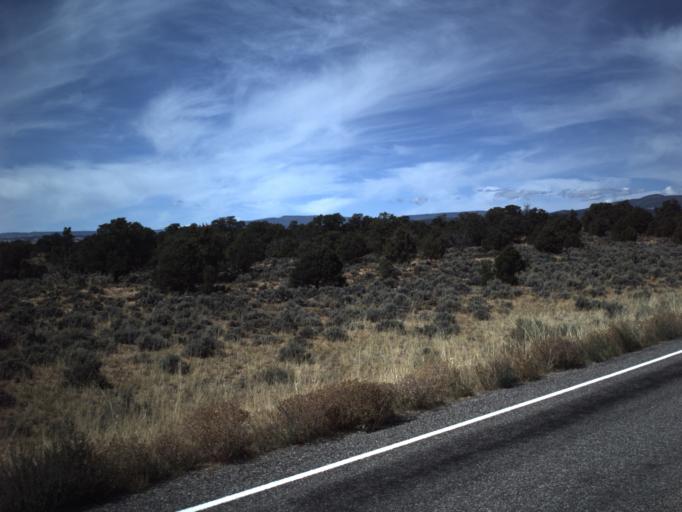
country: US
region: Utah
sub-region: Wayne County
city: Loa
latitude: 37.8525
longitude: -111.4312
